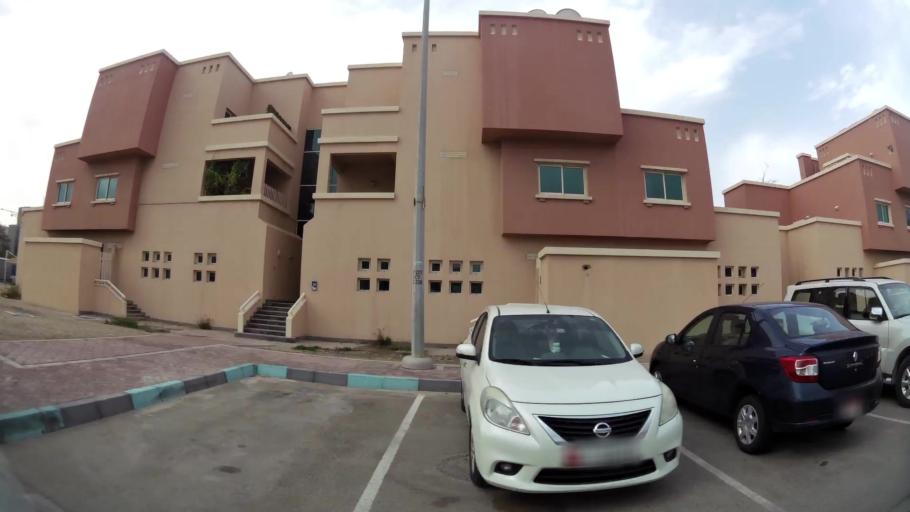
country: AE
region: Abu Dhabi
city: Abu Dhabi
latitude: 24.4755
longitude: 54.3821
